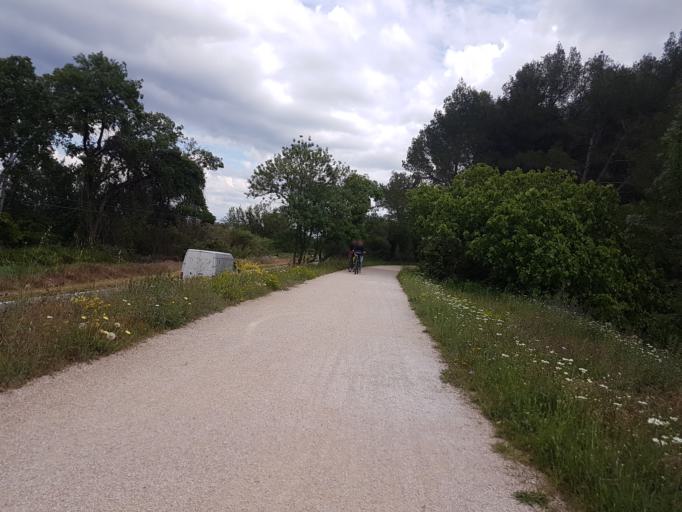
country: FR
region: Languedoc-Roussillon
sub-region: Departement du Gard
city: Vallabregues
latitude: 43.8269
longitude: 4.6242
